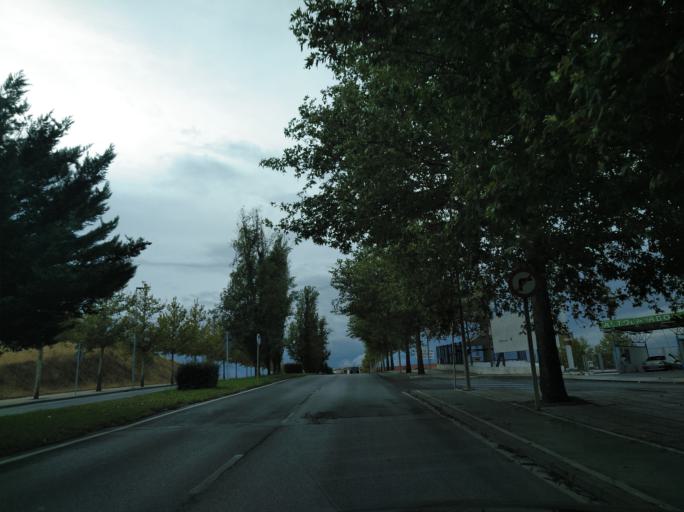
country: ES
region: Extremadura
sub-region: Provincia de Badajoz
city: Badajoz
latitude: 38.8627
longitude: -6.9737
